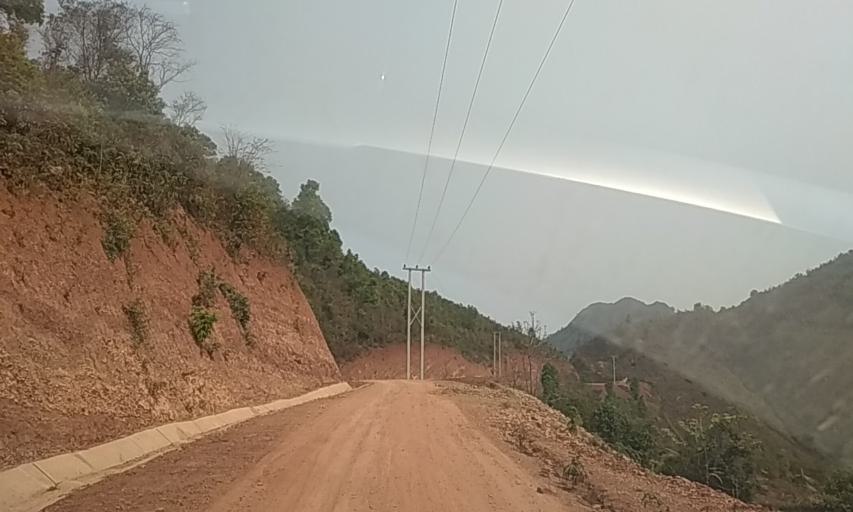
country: VN
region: Huyen Dien Bien
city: Dien Bien Phu
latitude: 21.4748
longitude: 102.7758
